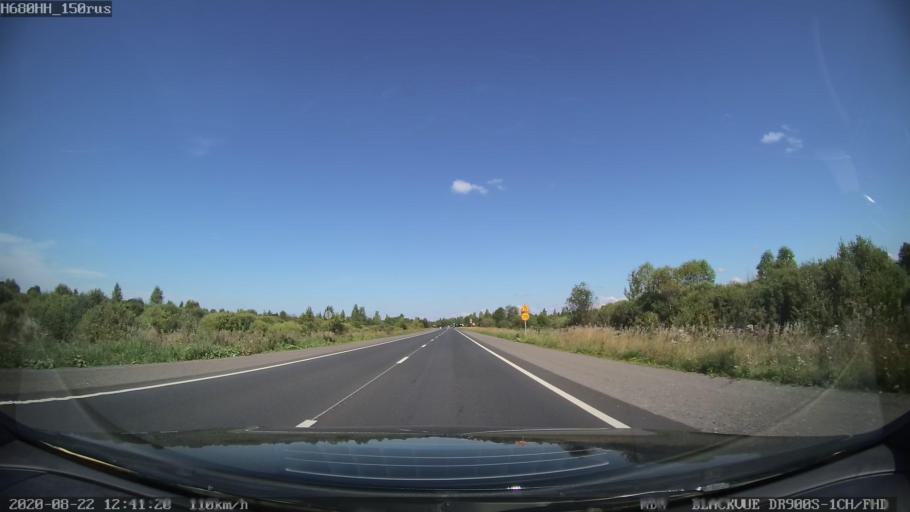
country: RU
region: Tverskaya
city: Rameshki
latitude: 57.3473
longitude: 36.0985
